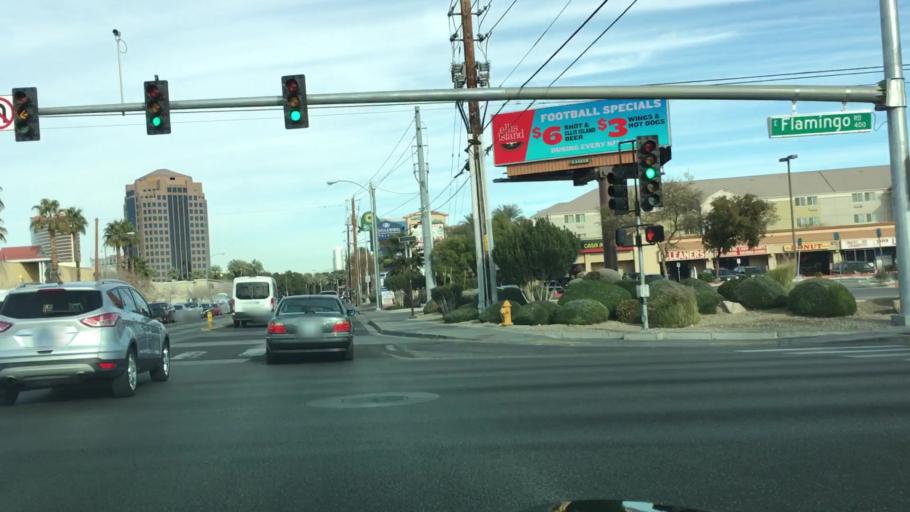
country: US
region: Nevada
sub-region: Clark County
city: Paradise
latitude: 36.1143
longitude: -115.1539
